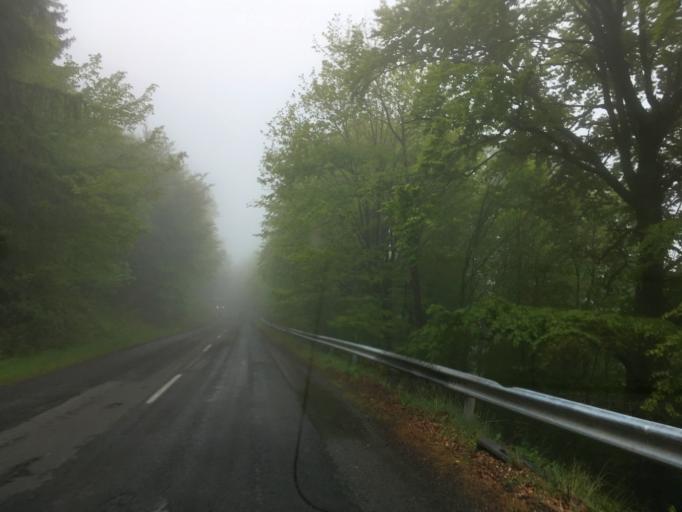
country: HU
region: Heves
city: Paradsasvar
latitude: 47.9159
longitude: 19.9122
